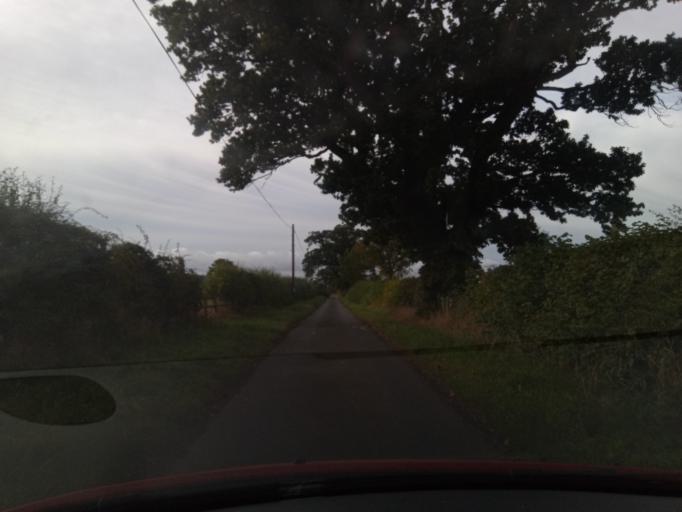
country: GB
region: Scotland
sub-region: The Scottish Borders
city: Kelso
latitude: 55.5897
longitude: -2.3975
